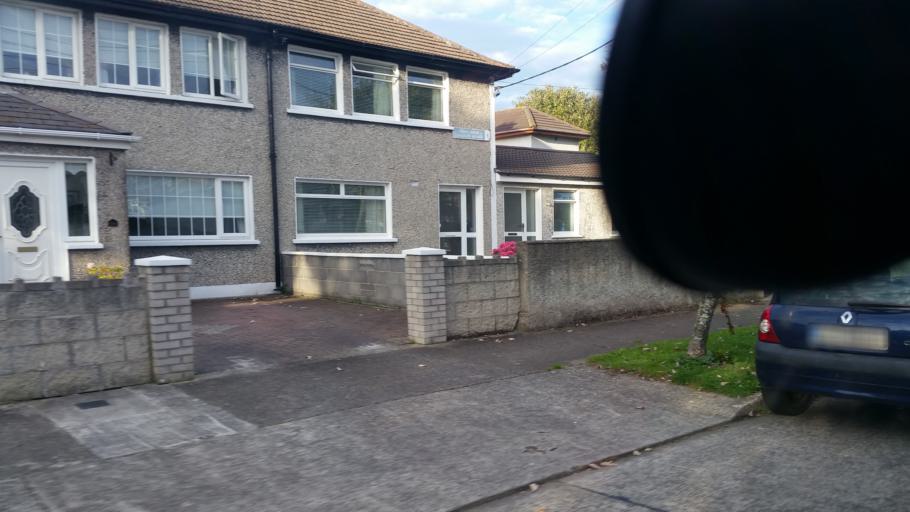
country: IE
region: Leinster
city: Beaumont
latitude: 53.3891
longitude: -6.2318
